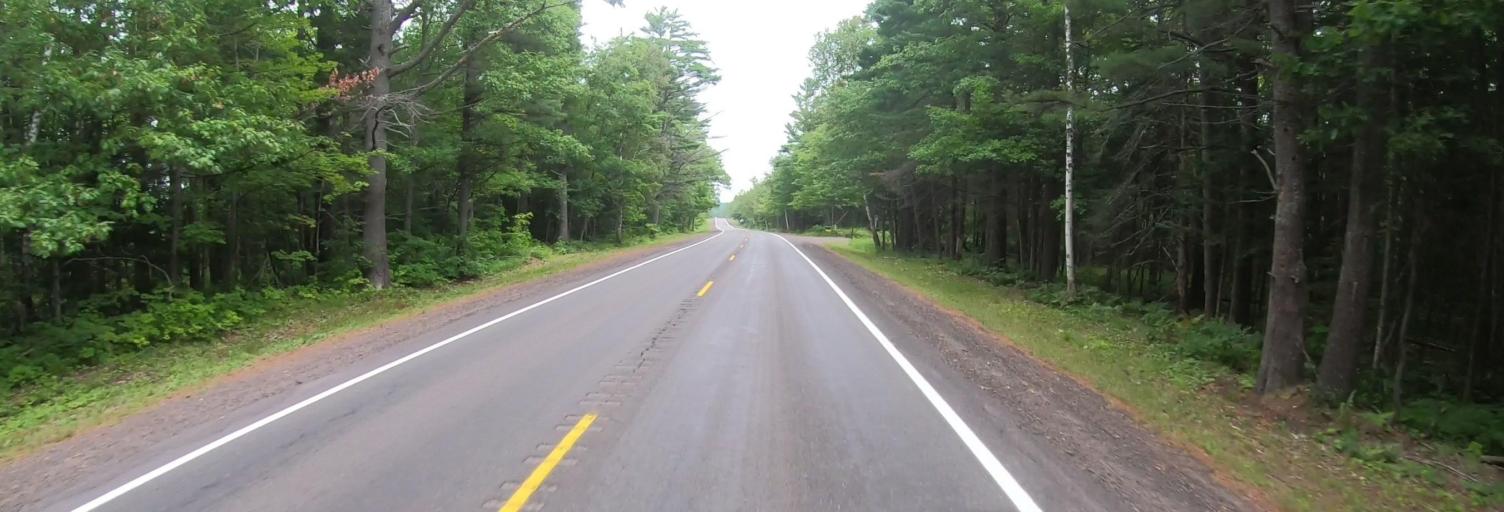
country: US
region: Michigan
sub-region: Keweenaw County
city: Eagle River
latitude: 47.3285
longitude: -88.3299
